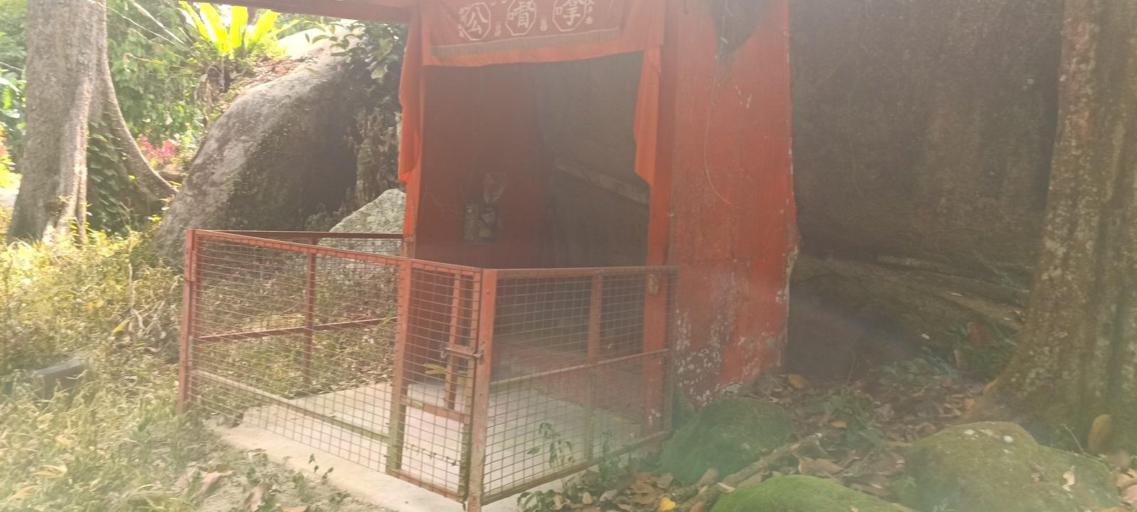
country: MY
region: Penang
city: Kampung Sungai Ara
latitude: 5.3291
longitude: 100.2540
